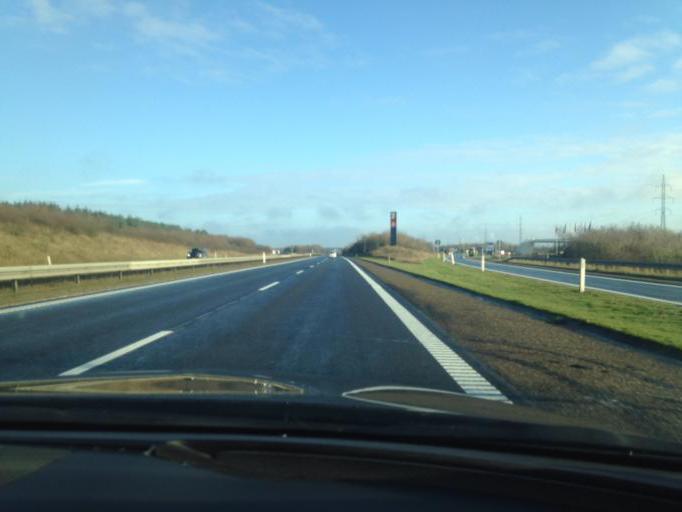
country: DK
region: South Denmark
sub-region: Kolding Kommune
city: Kolding
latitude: 55.5118
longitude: 9.3883
